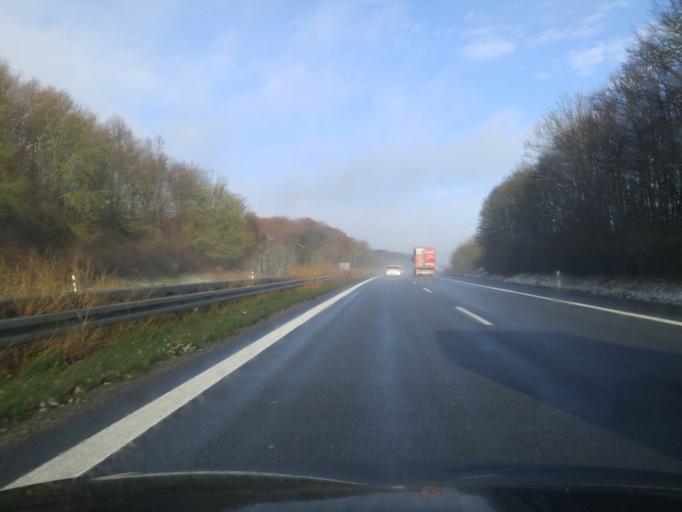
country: DE
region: Bavaria
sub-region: Regierungsbezirk Unterfranken
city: Rimpar
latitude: 49.8758
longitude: 9.9929
